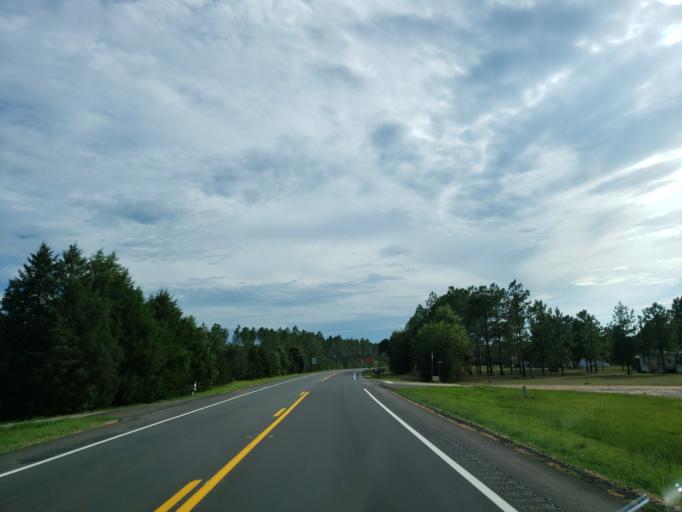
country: US
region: Georgia
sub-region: Berrien County
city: Enigma
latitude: 31.5427
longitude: -83.3843
